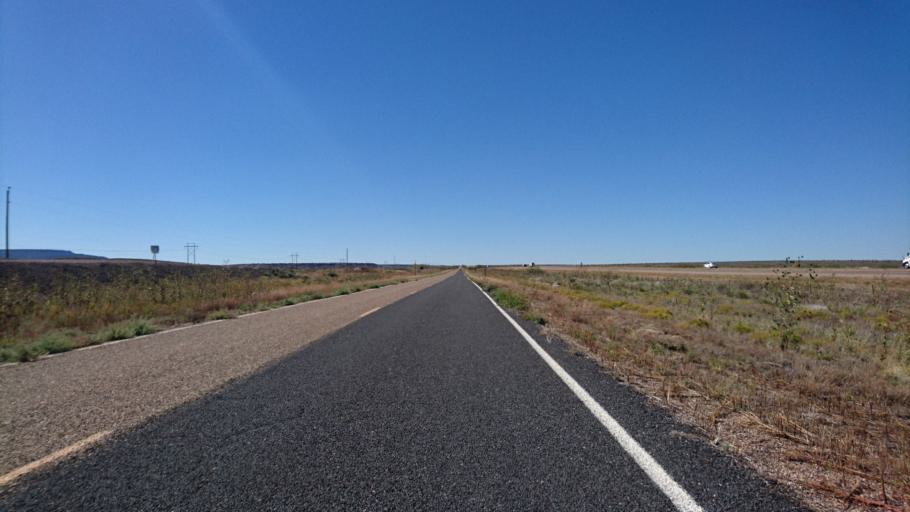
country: US
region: New Mexico
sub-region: Quay County
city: Tucumcari
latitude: 35.0870
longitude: -104.0944
